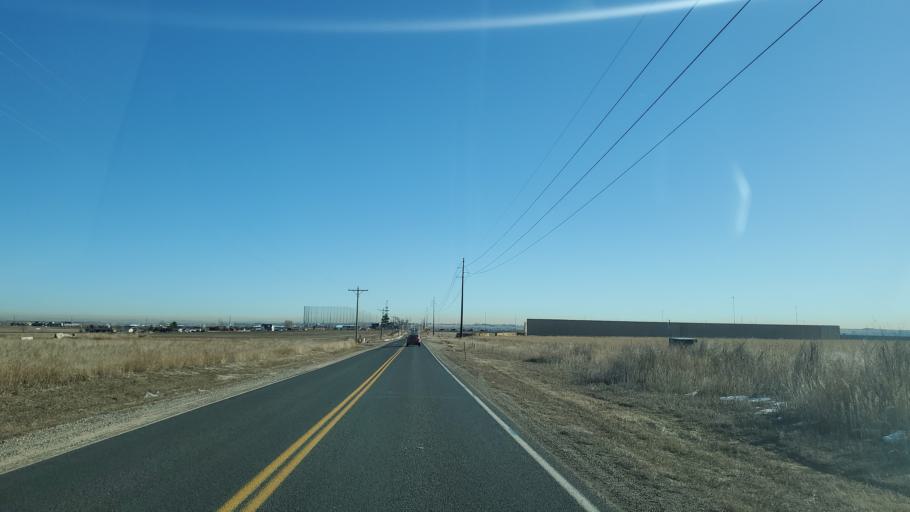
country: US
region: Colorado
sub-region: Boulder County
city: Erie
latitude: 39.9868
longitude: -105.0058
